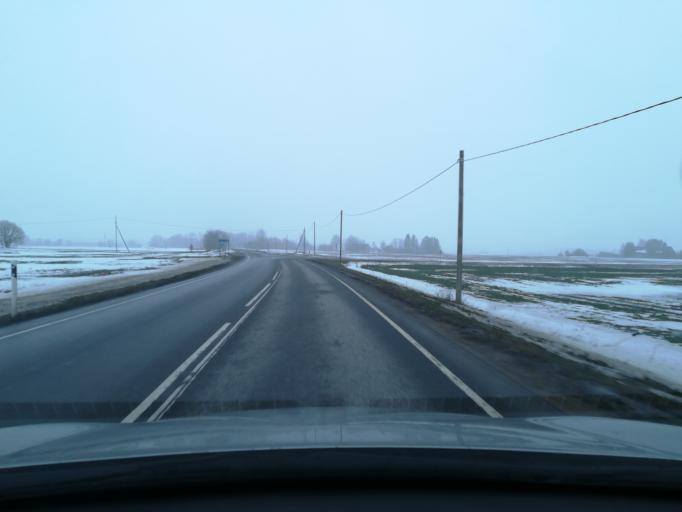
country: EE
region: Harju
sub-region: Raasiku vald
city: Raasiku
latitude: 59.3541
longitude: 25.1456
